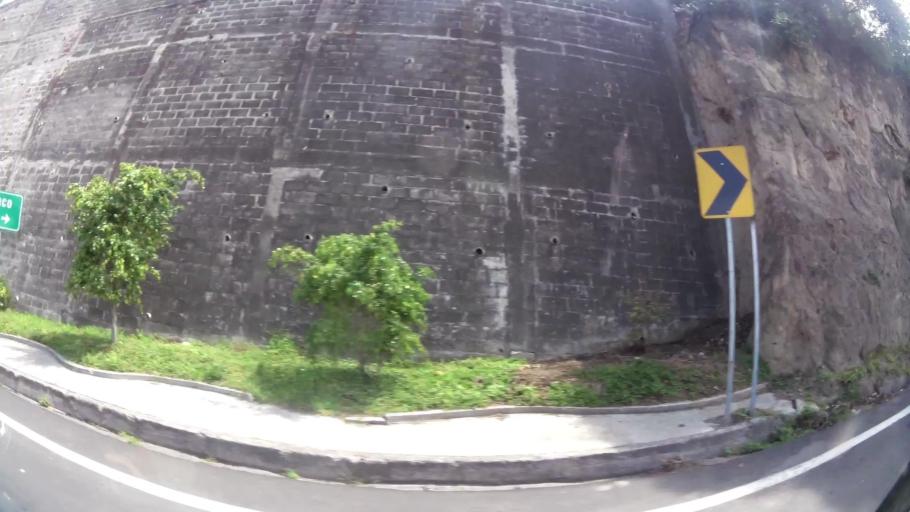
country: EC
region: Pichincha
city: Quito
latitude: -0.2039
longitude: -78.4324
